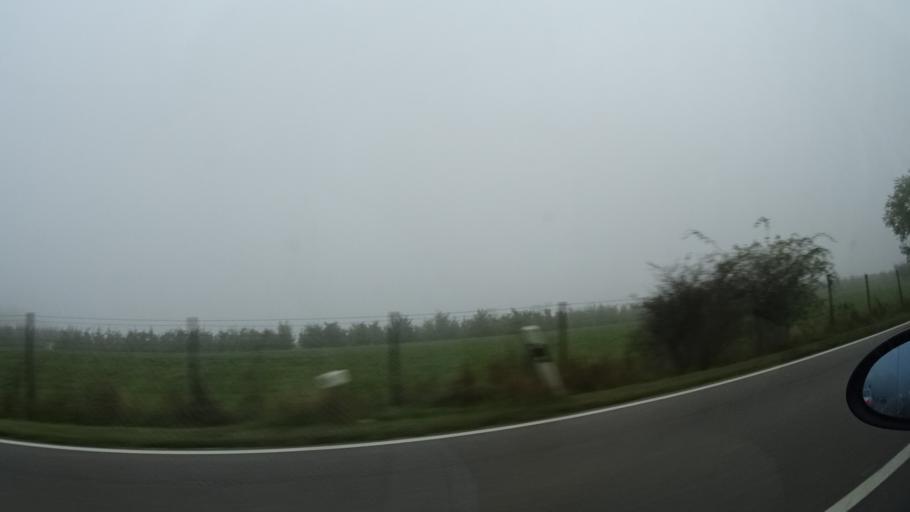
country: DE
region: Baden-Wuerttemberg
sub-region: Karlsruhe Region
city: Olbronn-Durrn
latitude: 48.9796
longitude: 8.7293
